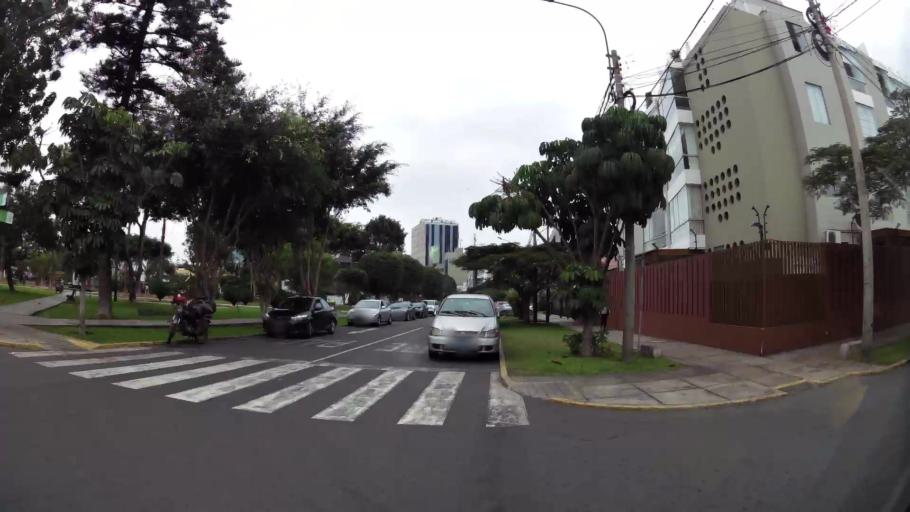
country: PE
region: Lima
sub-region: Lima
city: Surco
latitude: -12.1241
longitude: -77.0197
